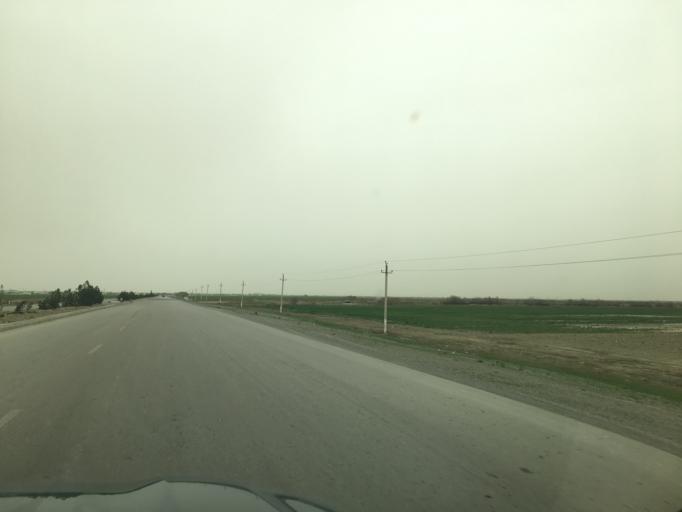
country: TM
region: Ahal
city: Baharly
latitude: 38.3838
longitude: 57.4970
